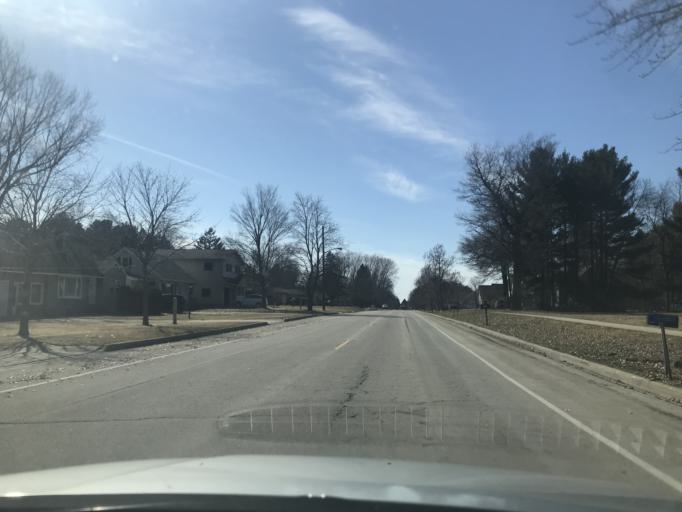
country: US
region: Wisconsin
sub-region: Marinette County
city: Marinette
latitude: 45.1117
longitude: -87.6382
